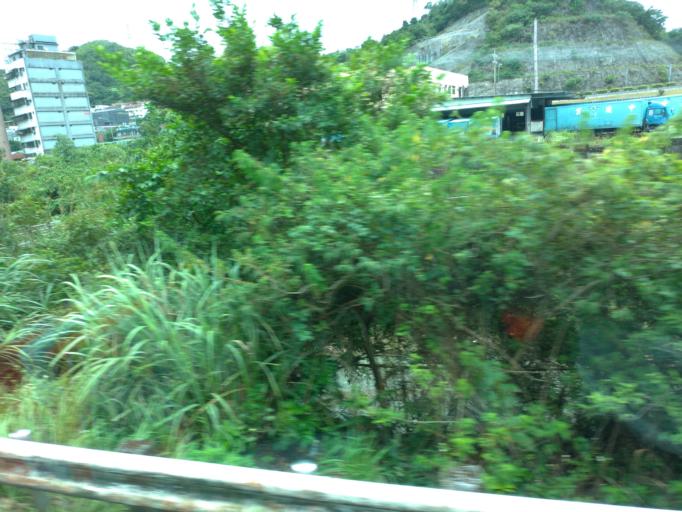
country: TW
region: Taiwan
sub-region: Keelung
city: Keelung
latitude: 25.1136
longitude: 121.7292
